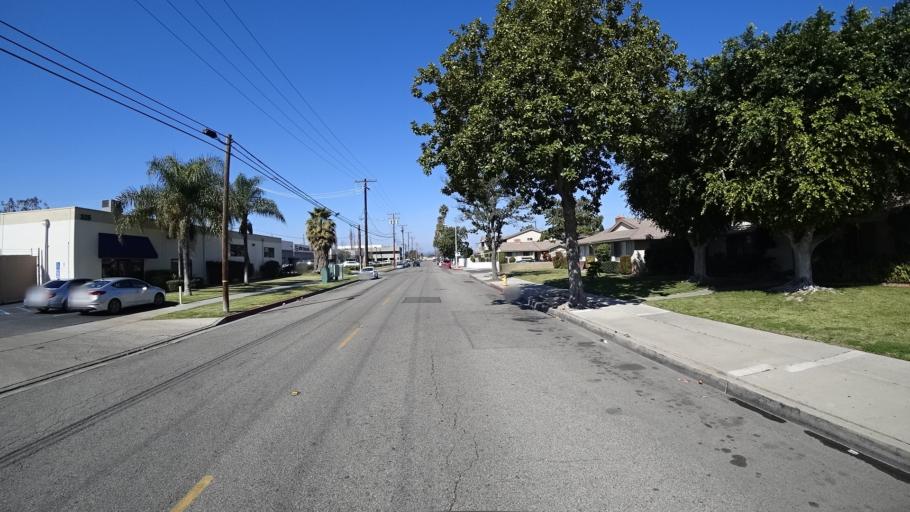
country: US
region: California
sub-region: Orange County
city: Anaheim
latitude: 33.8357
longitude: -117.9501
